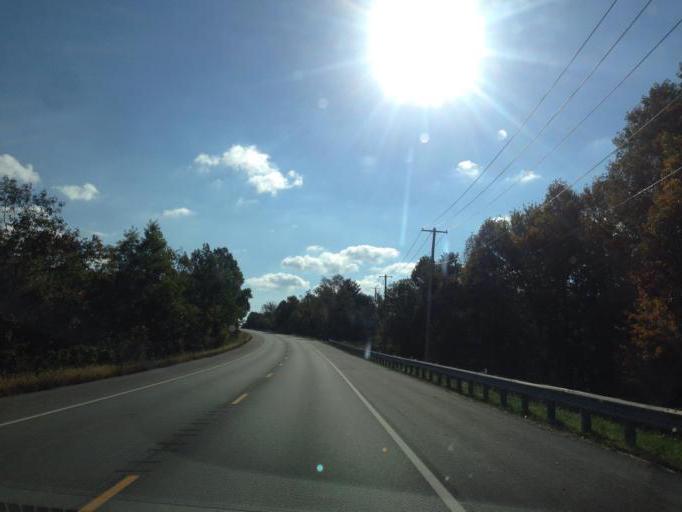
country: US
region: Maryland
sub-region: Carroll County
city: Mount Airy
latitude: 39.3553
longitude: -77.1374
